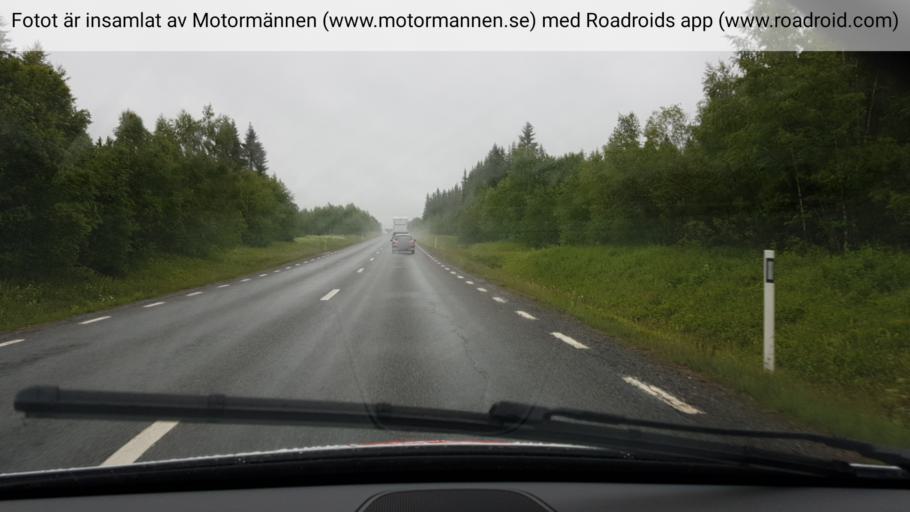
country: SE
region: Jaemtland
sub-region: OEstersunds Kommun
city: Lit
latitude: 63.4670
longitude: 15.1887
